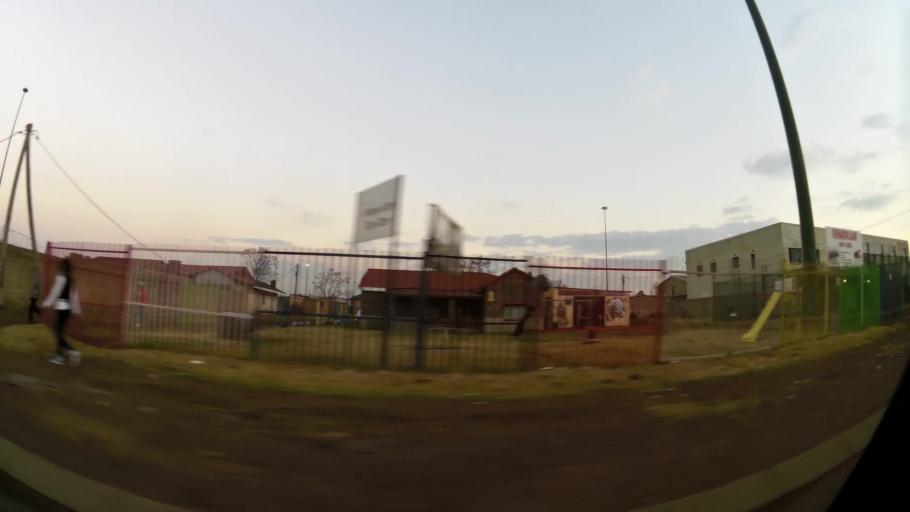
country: ZA
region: Gauteng
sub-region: City of Johannesburg Metropolitan Municipality
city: Orange Farm
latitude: -26.5468
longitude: 27.8385
